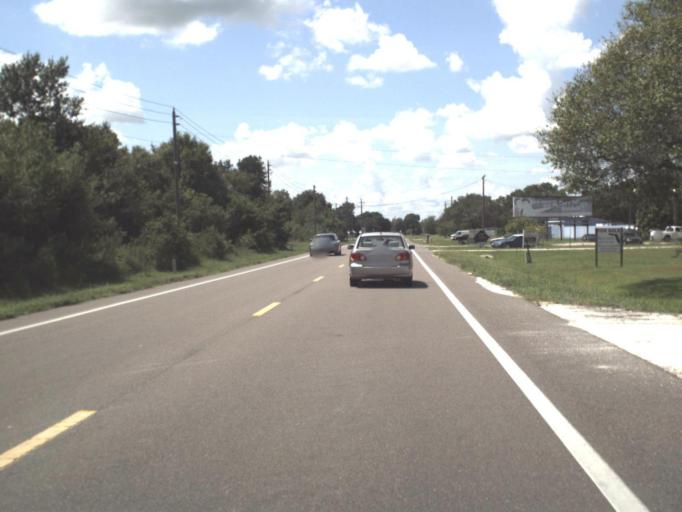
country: US
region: Florida
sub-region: DeSoto County
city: Nocatee
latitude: 27.1752
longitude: -81.8743
